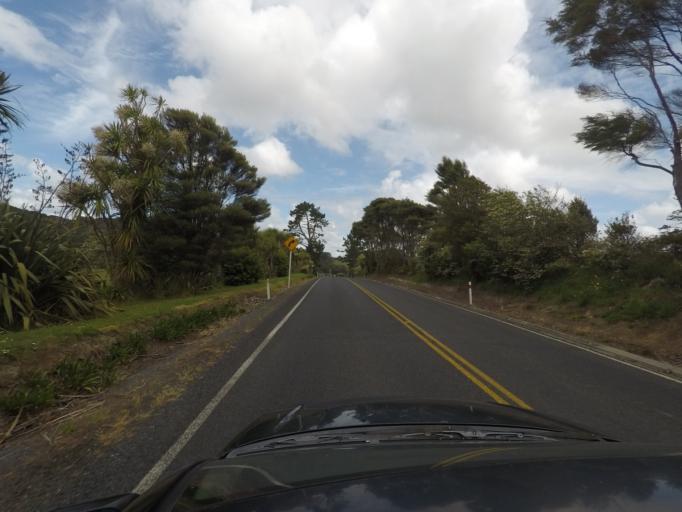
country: NZ
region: Auckland
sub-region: Auckland
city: Parakai
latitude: -36.6474
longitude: 174.5182
